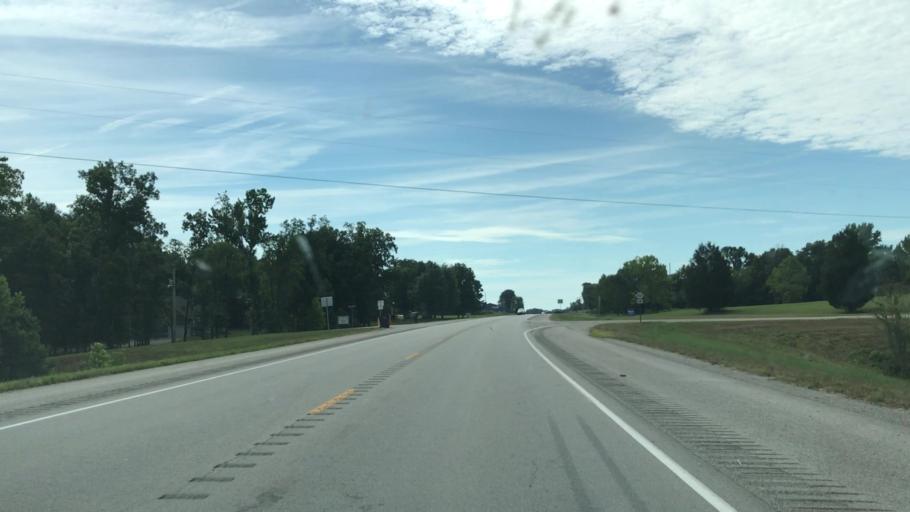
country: US
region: Kentucky
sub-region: Edmonson County
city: Brownsville
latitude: 37.1736
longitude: -86.2355
